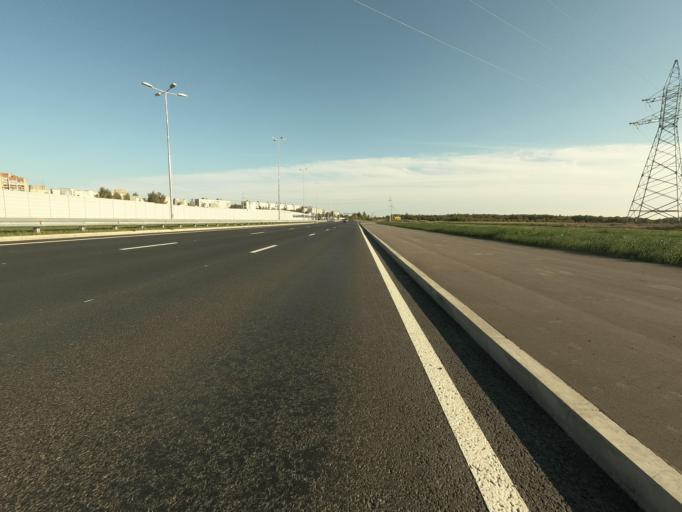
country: RU
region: St.-Petersburg
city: Kolpino
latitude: 59.7384
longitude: 30.5524
